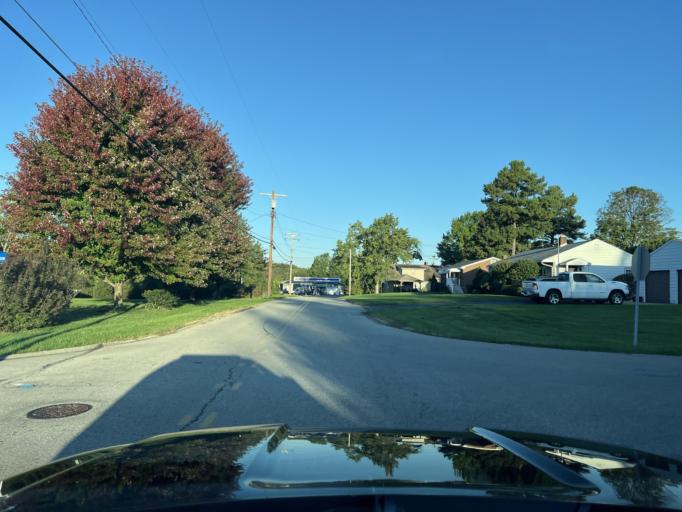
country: US
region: Pennsylvania
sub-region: Fayette County
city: Leith-Hatfield
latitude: 39.8708
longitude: -79.7403
